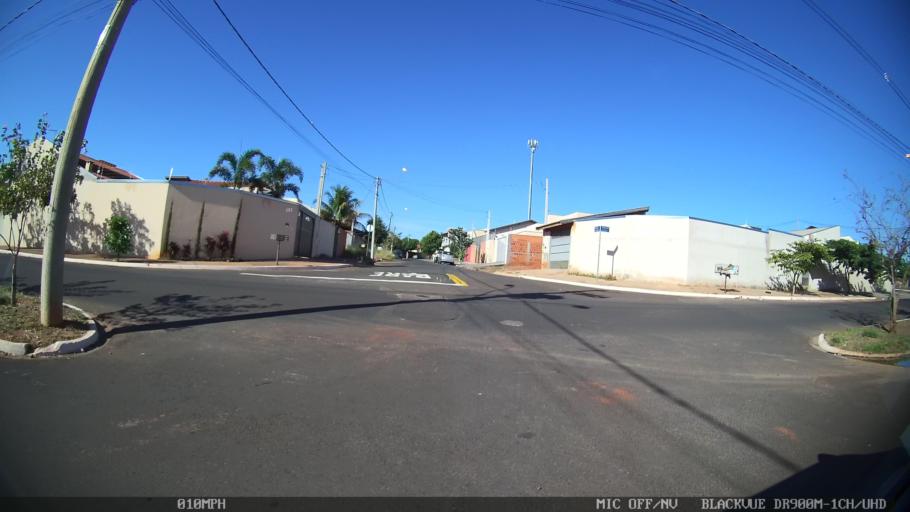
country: BR
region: Sao Paulo
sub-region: Olimpia
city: Olimpia
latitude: -20.7391
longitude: -48.8826
